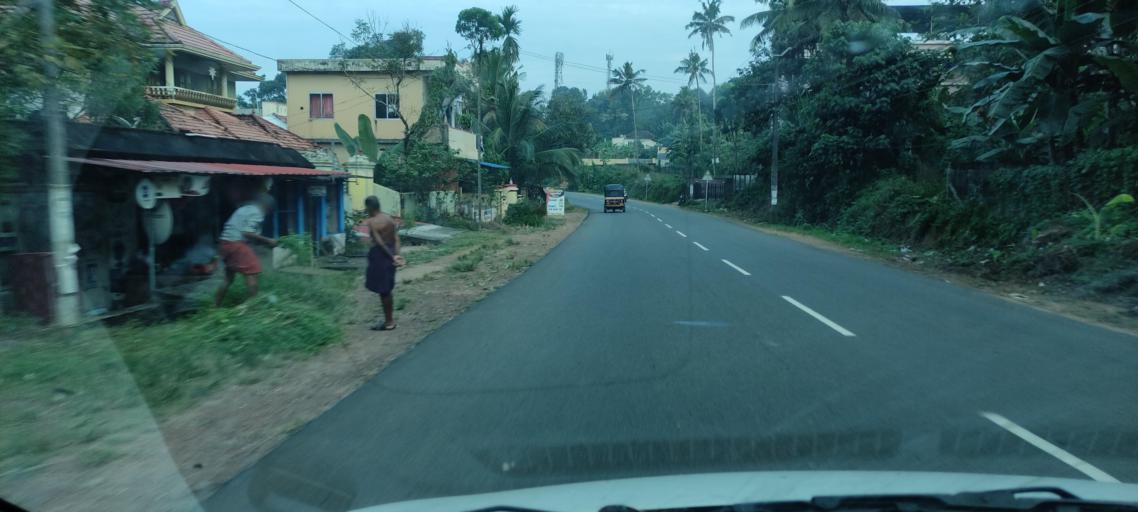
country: IN
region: Kerala
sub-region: Pattanamtitta
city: Adur
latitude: 9.1322
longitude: 76.7143
